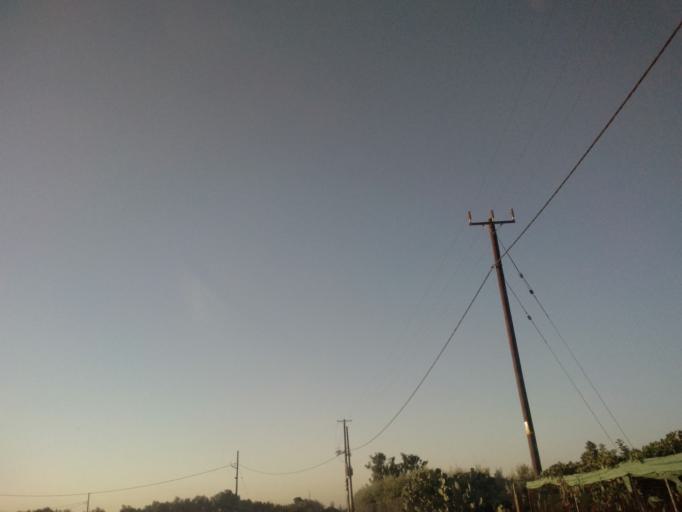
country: CY
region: Limassol
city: Ypsonas
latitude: 34.6716
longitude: 32.9592
